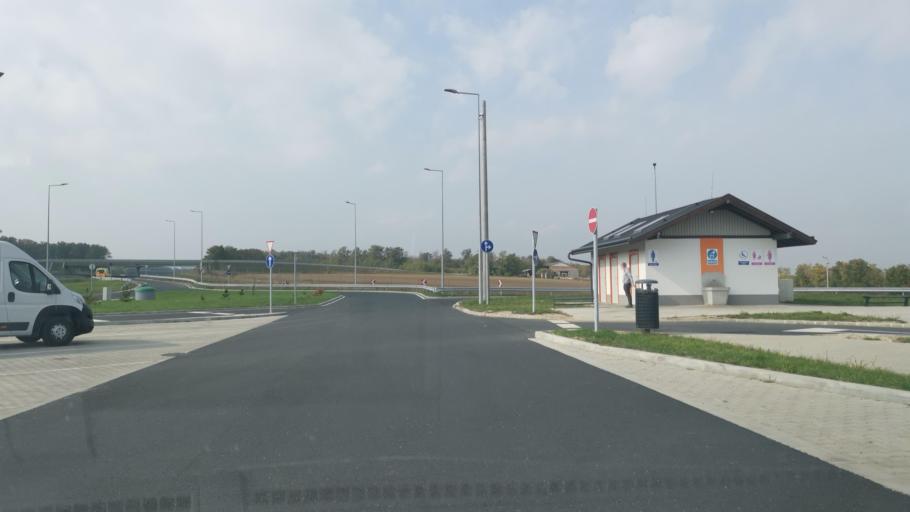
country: AT
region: Burgenland
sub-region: Politischer Bezirk Oberpullendorf
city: Deutschkreutz
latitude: 47.6283
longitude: 16.6471
